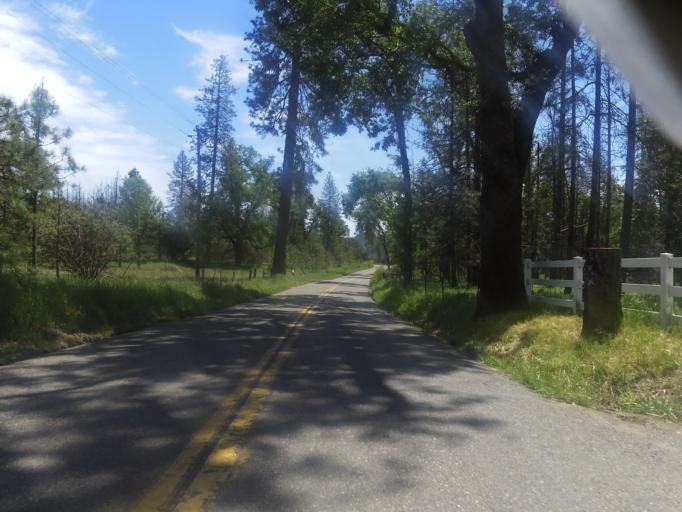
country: US
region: California
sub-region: Mariposa County
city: Midpines
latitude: 37.4841
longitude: -119.8116
